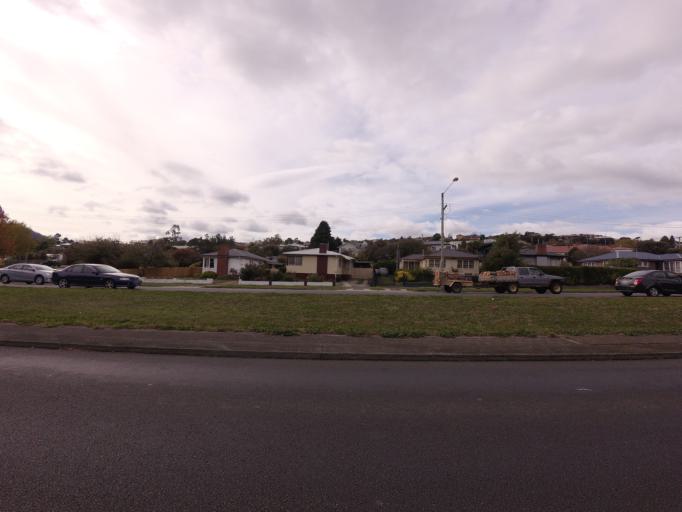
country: AU
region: Tasmania
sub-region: Glenorchy
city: Moonah
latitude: -42.8401
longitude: 147.3047
